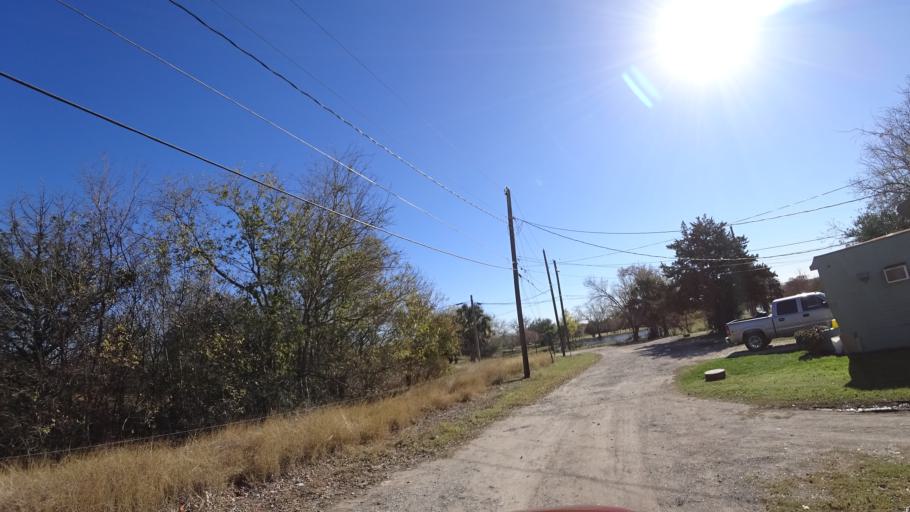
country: US
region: Texas
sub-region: Travis County
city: Garfield
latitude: 30.1196
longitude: -97.6364
